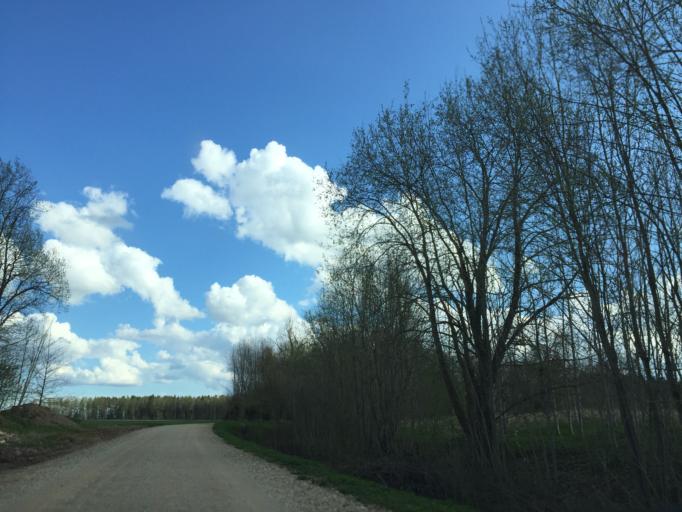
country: LV
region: Beverina
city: Murmuiza
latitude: 57.4319
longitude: 25.5469
